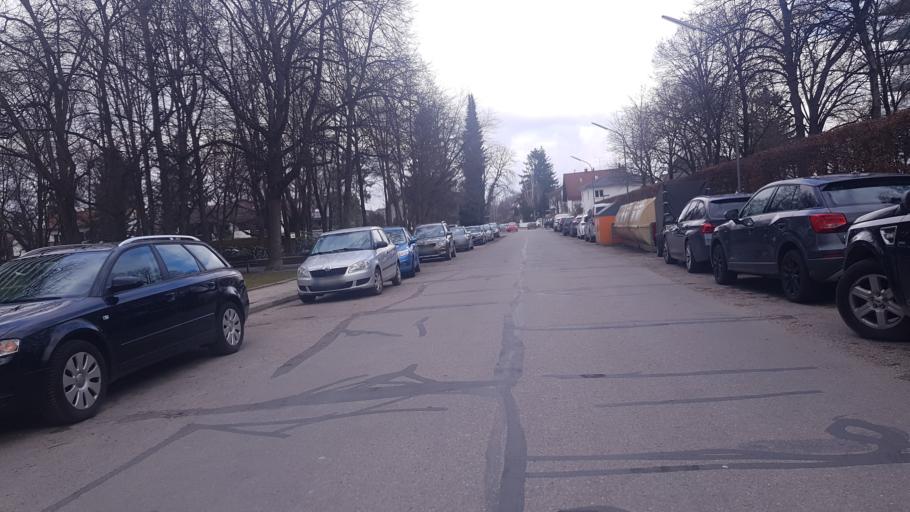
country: DE
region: Bavaria
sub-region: Upper Bavaria
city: Bogenhausen
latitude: 48.1558
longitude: 11.6322
